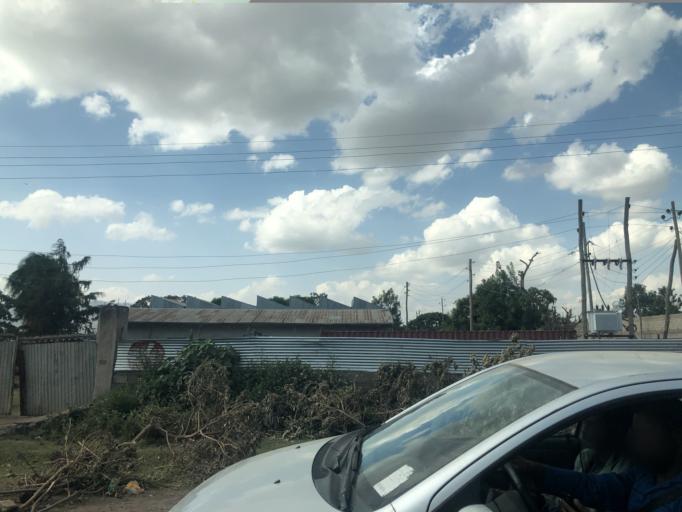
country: ET
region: Southern Nations, Nationalities, and People's Region
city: K'olito
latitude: 7.3012
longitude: 38.0850
